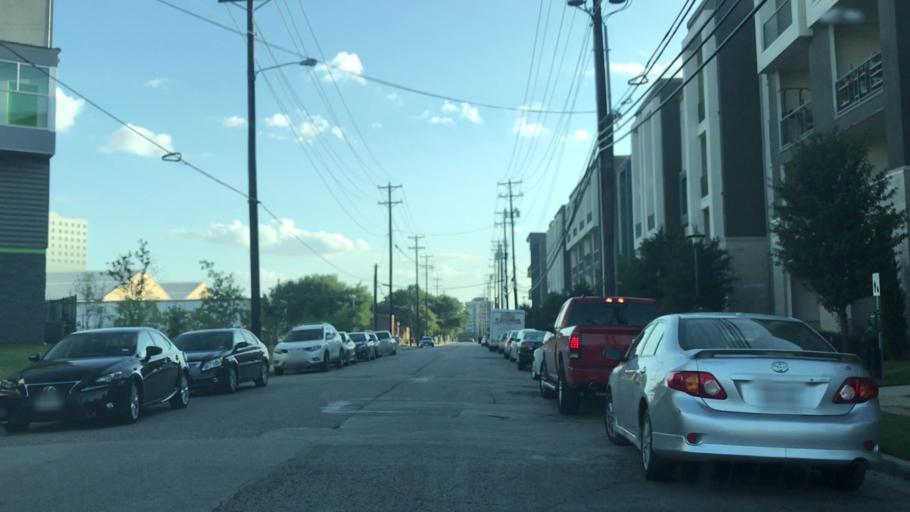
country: US
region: Texas
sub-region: Dallas County
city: Highland Park
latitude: 32.8185
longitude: -96.8338
